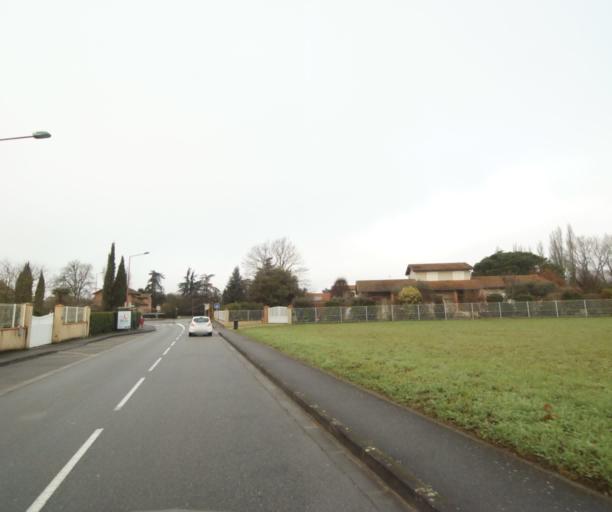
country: FR
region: Midi-Pyrenees
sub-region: Departement de la Haute-Garonne
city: Villemur-sur-Tarn
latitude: 43.8652
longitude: 1.4994
